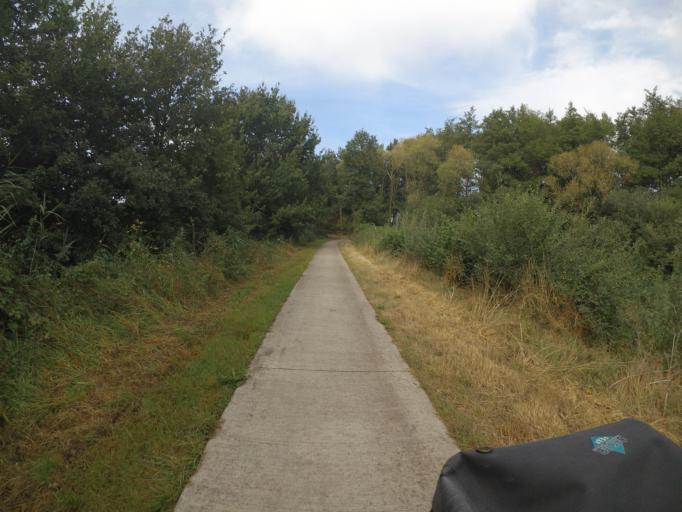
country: NL
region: Gelderland
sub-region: Gemeente Brummen
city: Eerbeek
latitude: 52.1599
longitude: 6.0627
